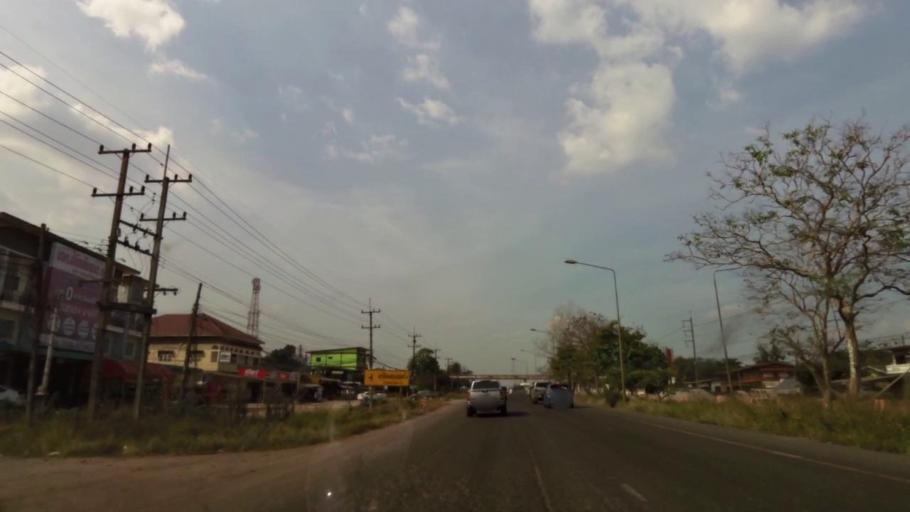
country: TH
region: Rayong
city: Klaeng
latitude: 12.8168
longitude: 101.6338
